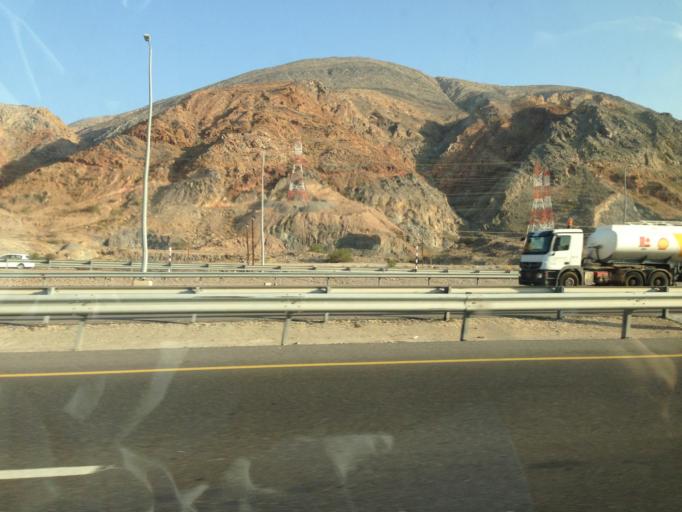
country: OM
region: Muhafazat Masqat
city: Bawshar
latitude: 23.5789
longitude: 58.4399
